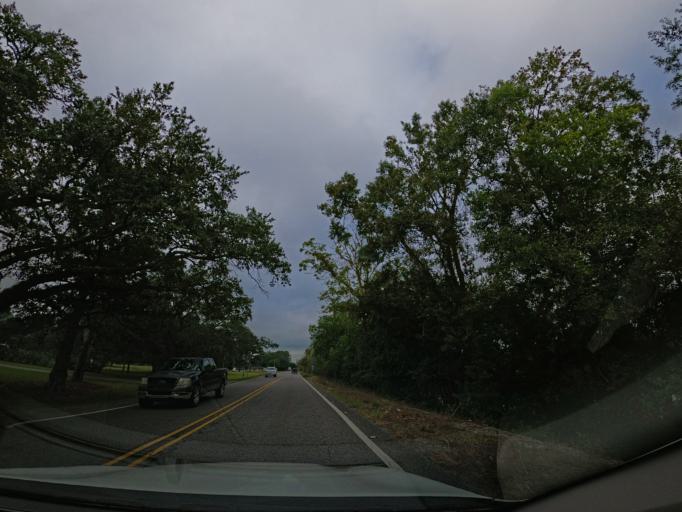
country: US
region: Louisiana
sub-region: Terrebonne Parish
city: Houma
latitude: 29.5742
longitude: -90.7562
